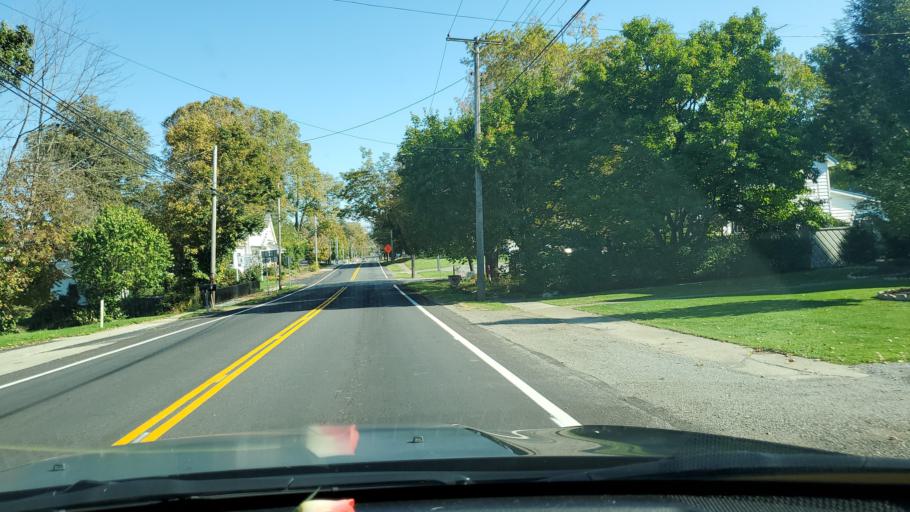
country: US
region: Ohio
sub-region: Ashtabula County
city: Andover
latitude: 41.4450
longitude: -80.5878
